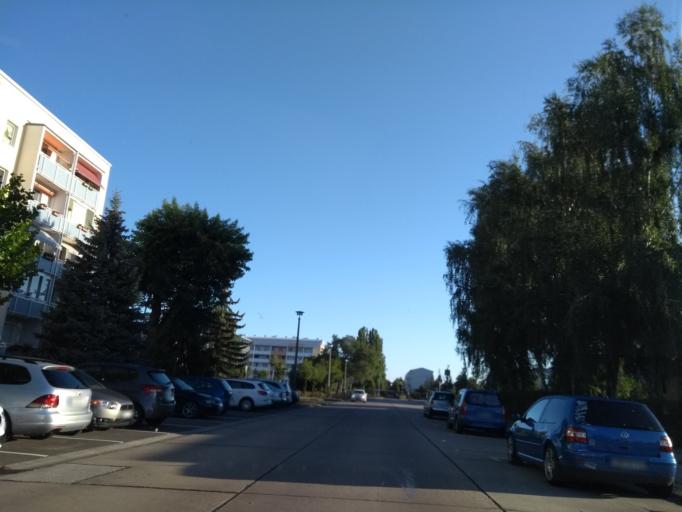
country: DE
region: Brandenburg
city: Lubbenau
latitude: 51.8588
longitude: 13.9444
